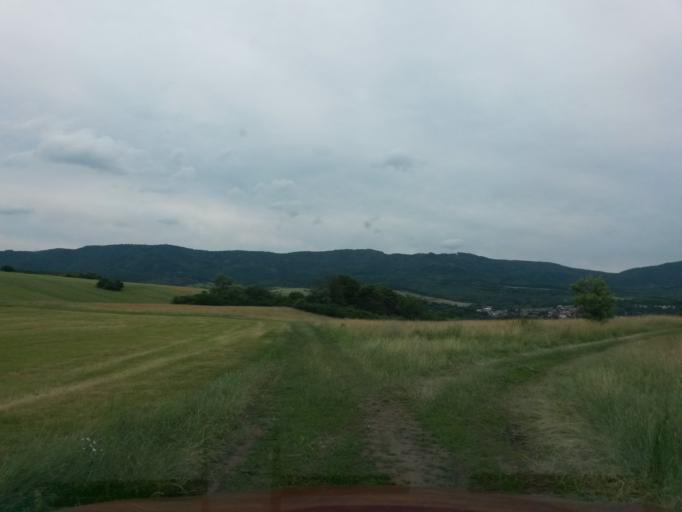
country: SK
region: Nitriansky
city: Handlova
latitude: 48.7433
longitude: 18.7515
